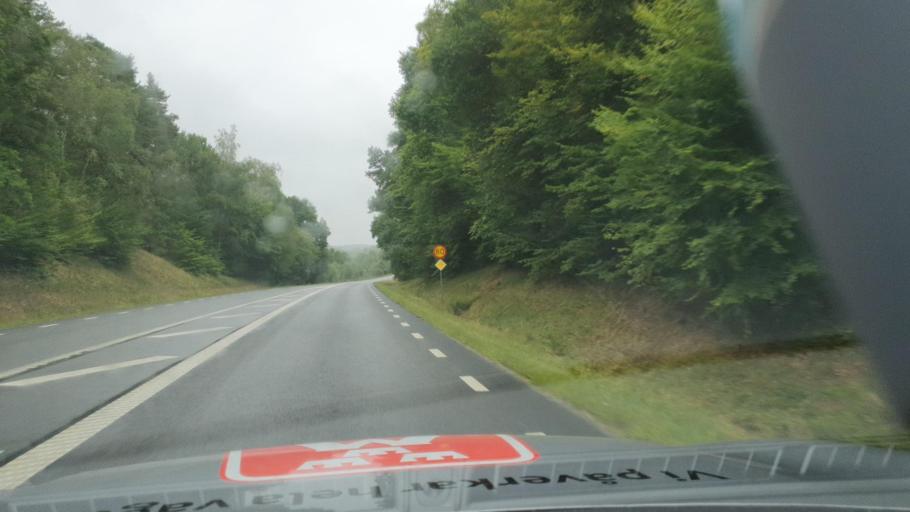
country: SE
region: Skane
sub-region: Hassleholms Kommun
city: Tormestorp
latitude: 56.1020
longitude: 13.7375
